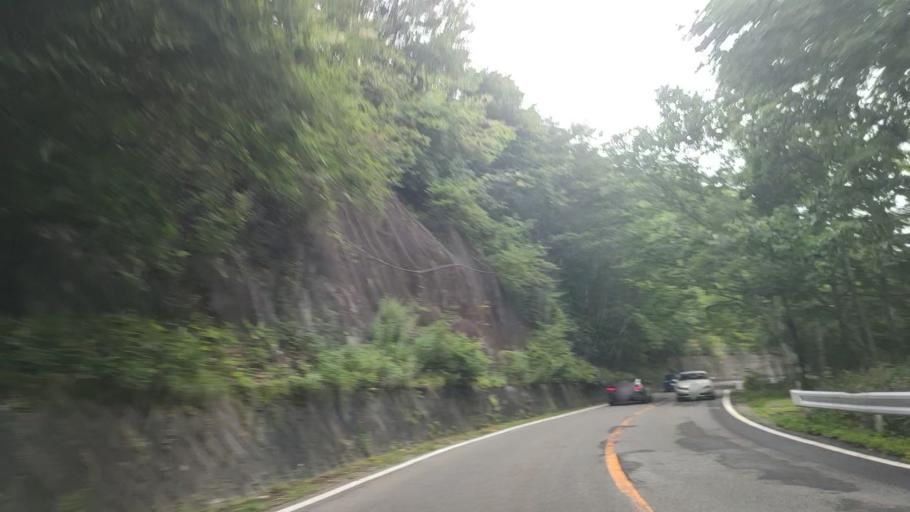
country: JP
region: Tochigi
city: Nikko
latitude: 36.8109
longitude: 139.4182
